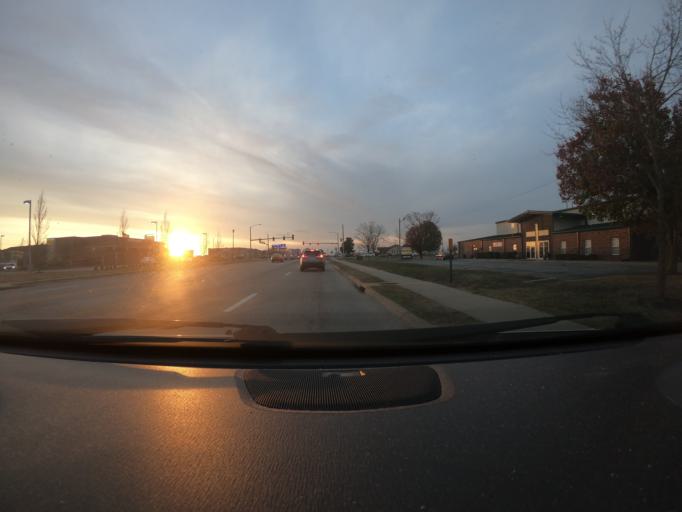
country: US
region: Arkansas
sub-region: Benton County
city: Bentonville
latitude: 36.3357
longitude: -94.2209
